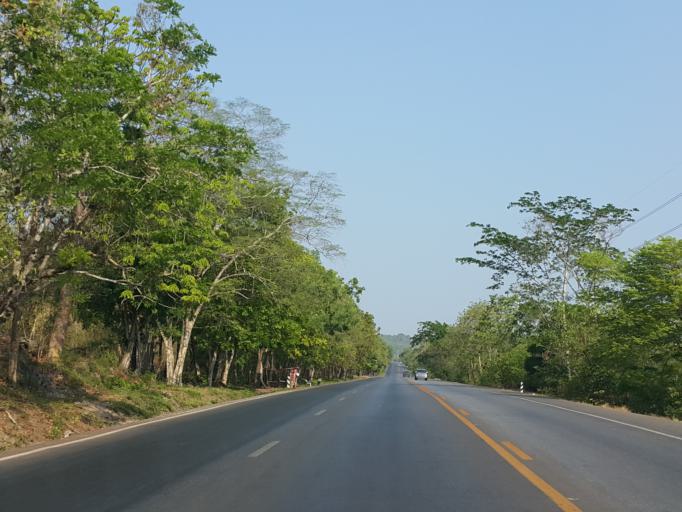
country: TH
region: Kanchanaburi
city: Sai Yok
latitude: 14.1071
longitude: 99.2173
